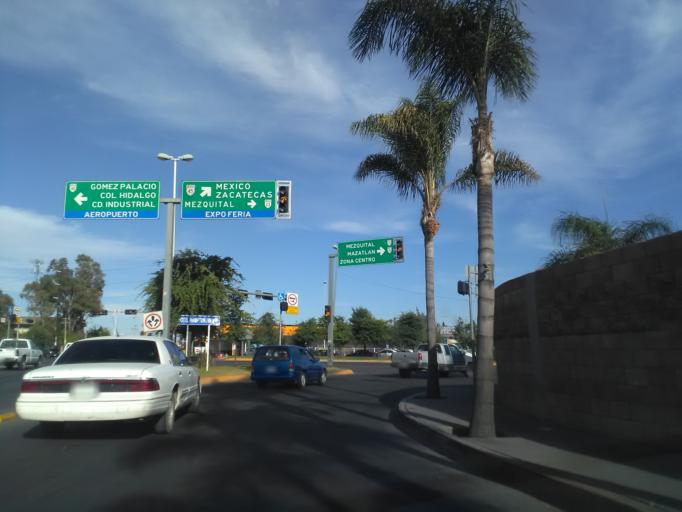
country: MX
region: Durango
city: Victoria de Durango
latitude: 24.0352
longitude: -104.6374
